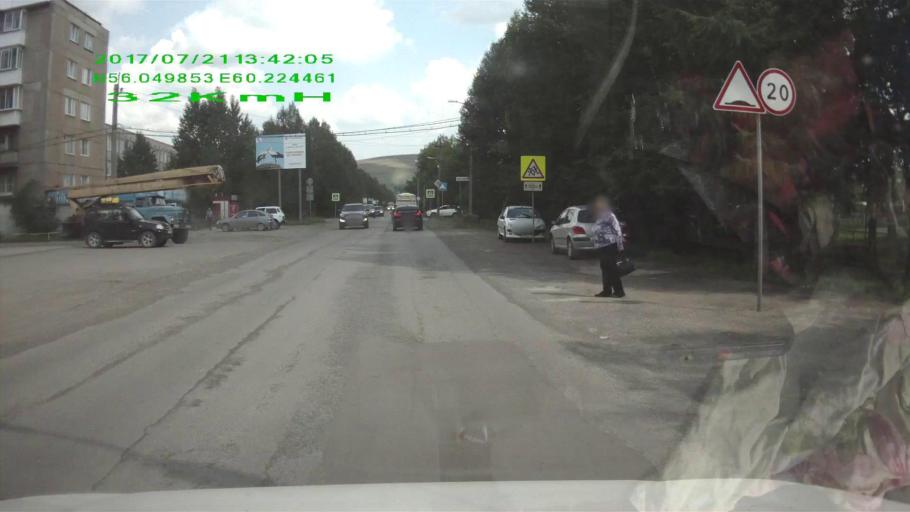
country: RU
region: Chelyabinsk
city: Verkhniy Ufaley
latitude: 56.0499
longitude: 60.2245
